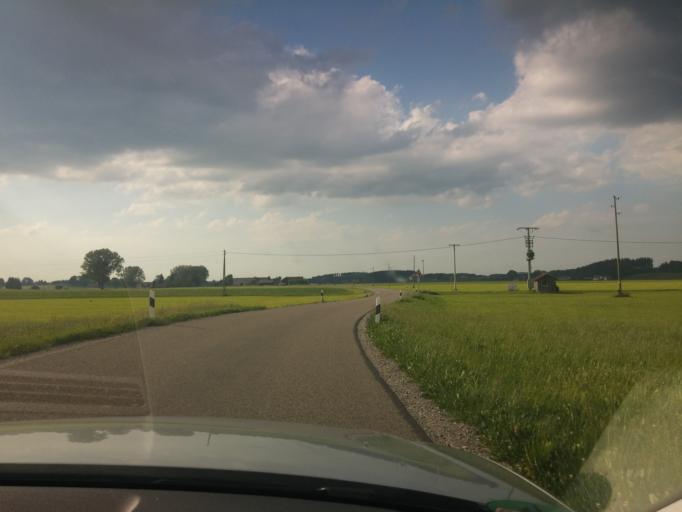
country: DE
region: Bavaria
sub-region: Swabia
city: Legau
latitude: 47.8324
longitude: 10.1725
